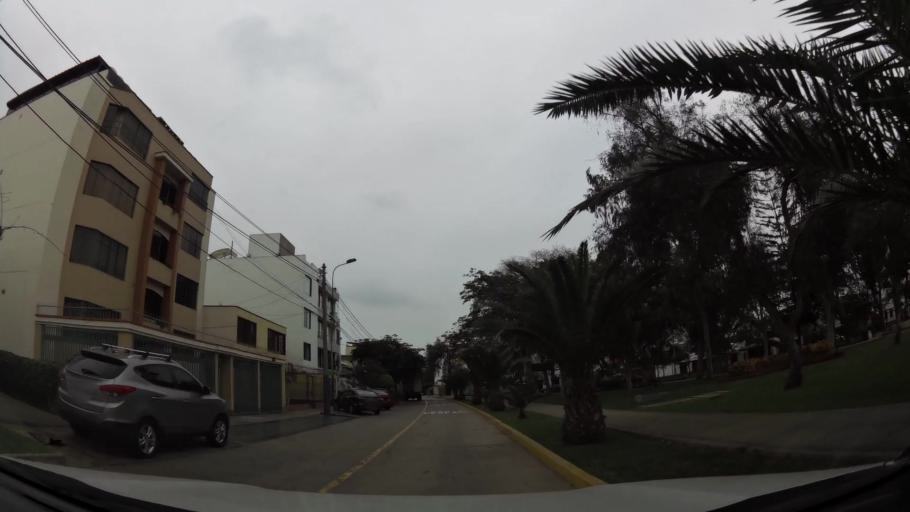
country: PE
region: Lima
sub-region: Lima
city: San Luis
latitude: -12.0988
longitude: -77.0075
